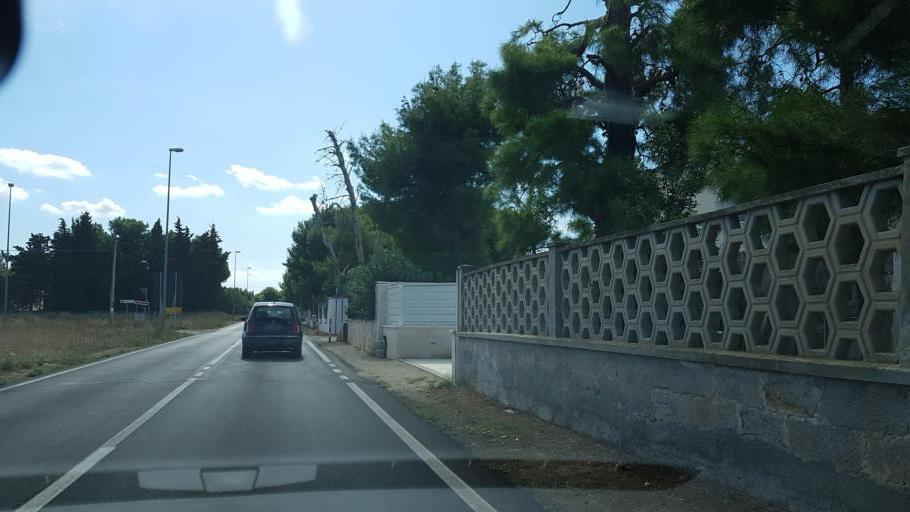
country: IT
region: Apulia
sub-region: Provincia di Lecce
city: Porto Cesareo
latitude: 40.2456
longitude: 17.9134
